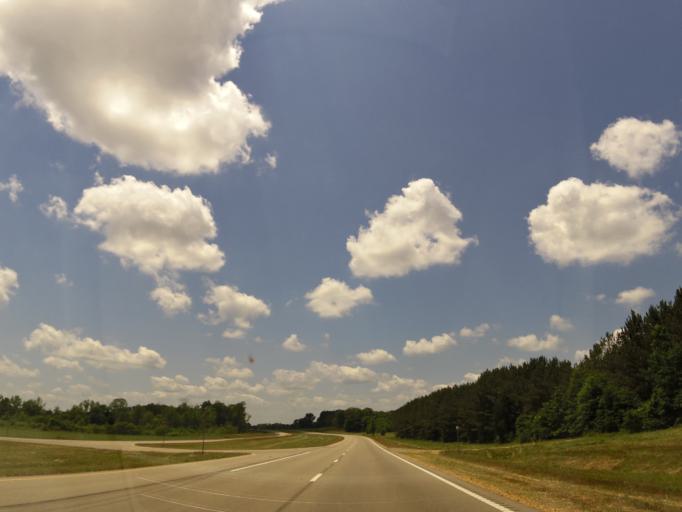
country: US
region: Mississippi
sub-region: Lee County
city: Verona
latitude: 34.2203
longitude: -88.8301
